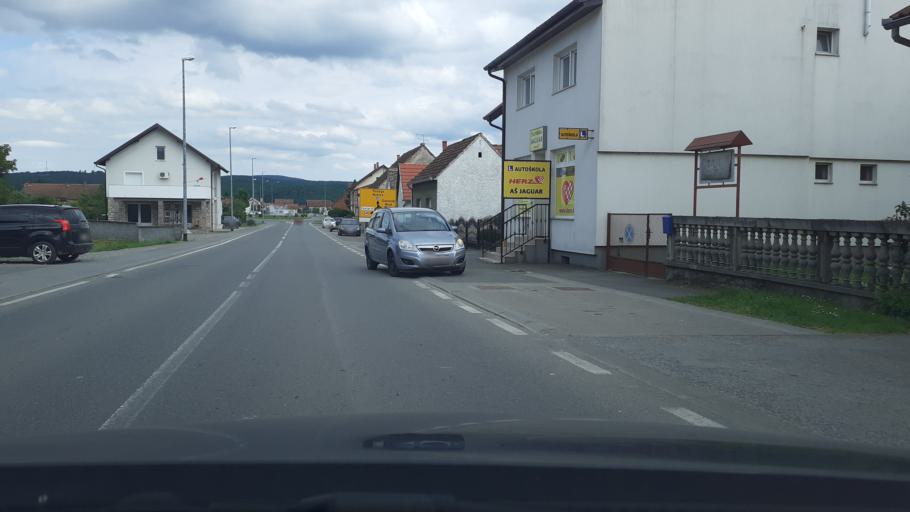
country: HR
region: Pozesko-Slavonska
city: Pleternica
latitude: 45.2837
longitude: 17.8015
